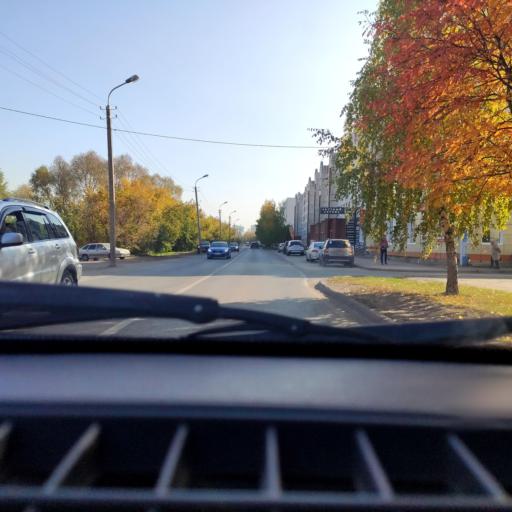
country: RU
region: Bashkortostan
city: Mikhaylovka
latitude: 54.7092
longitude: 55.8380
